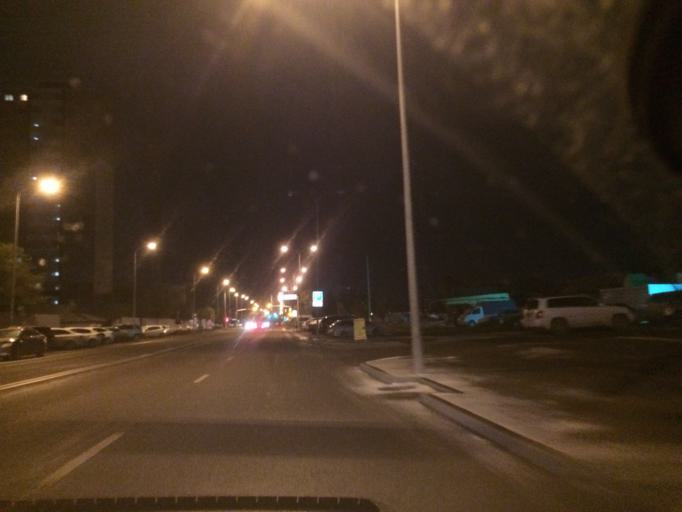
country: KZ
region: Astana Qalasy
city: Astana
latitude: 51.1621
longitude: 71.4554
